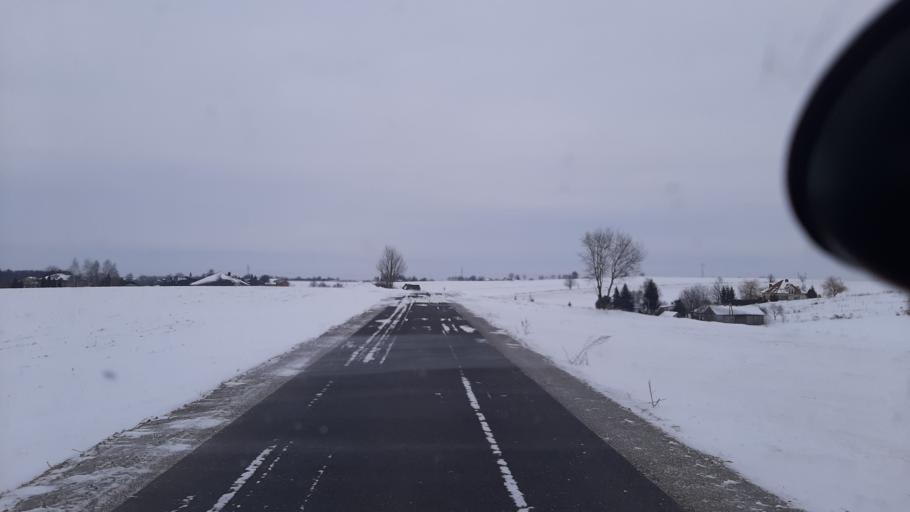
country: PL
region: Lublin Voivodeship
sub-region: Powiat lubelski
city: Garbow
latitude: 51.3362
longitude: 22.2923
